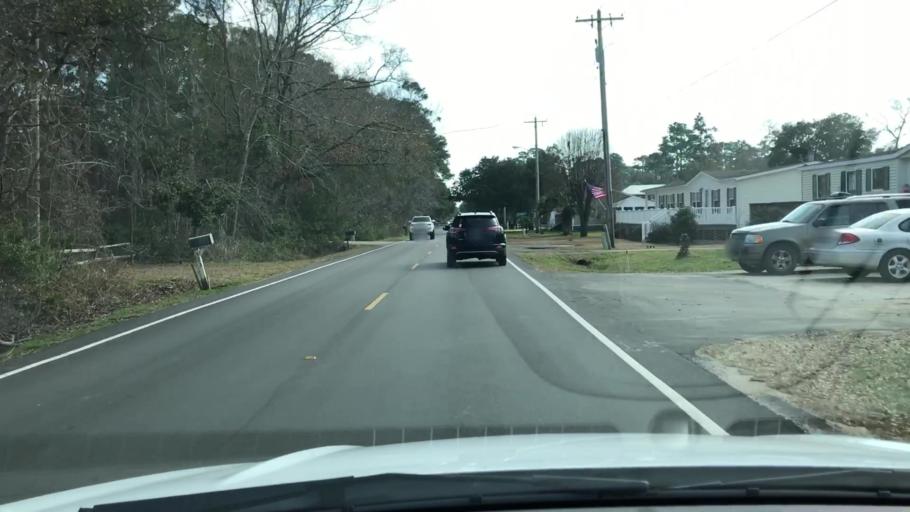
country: US
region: South Carolina
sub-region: Horry County
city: Garden City
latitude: 33.5880
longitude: -79.0036
